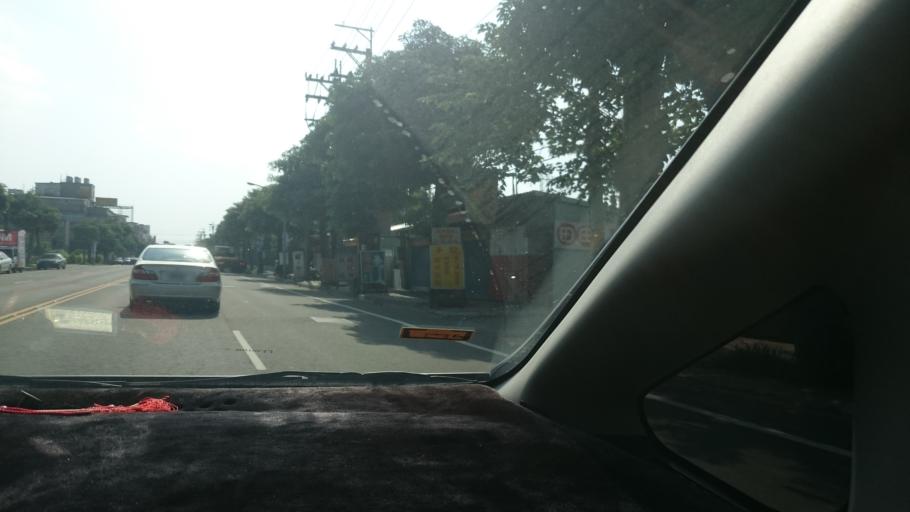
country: TW
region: Taiwan
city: Daxi
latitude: 24.9071
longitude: 121.2784
